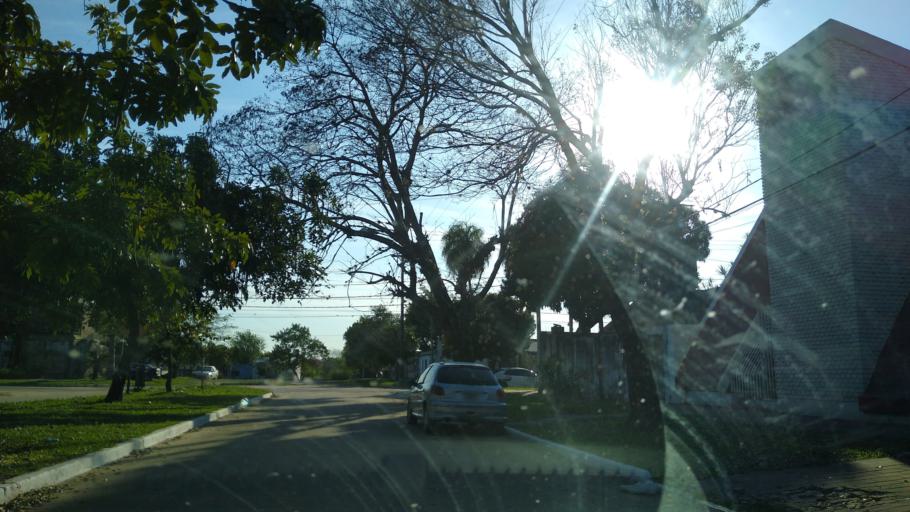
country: AR
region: Chaco
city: Barranqueras
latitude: -27.4785
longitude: -58.9528
